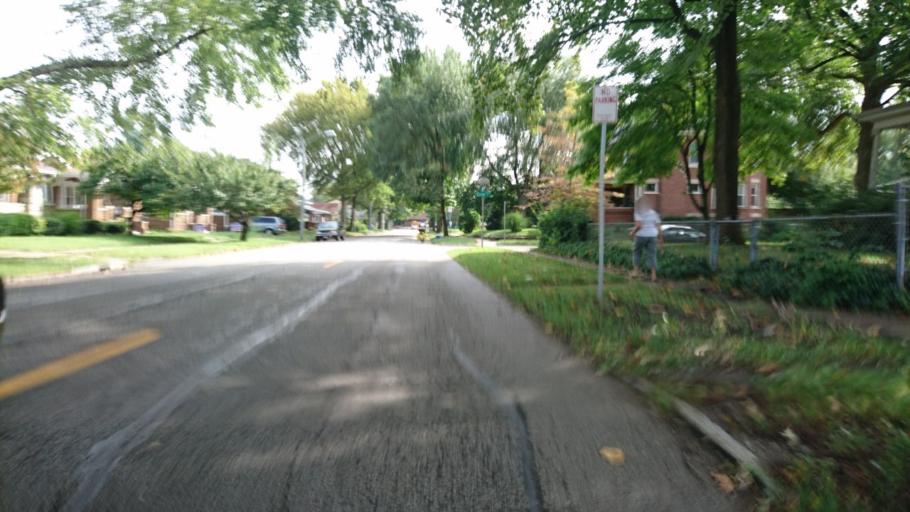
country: US
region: Illinois
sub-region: Sangamon County
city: Springfield
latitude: 39.7849
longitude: -89.6537
